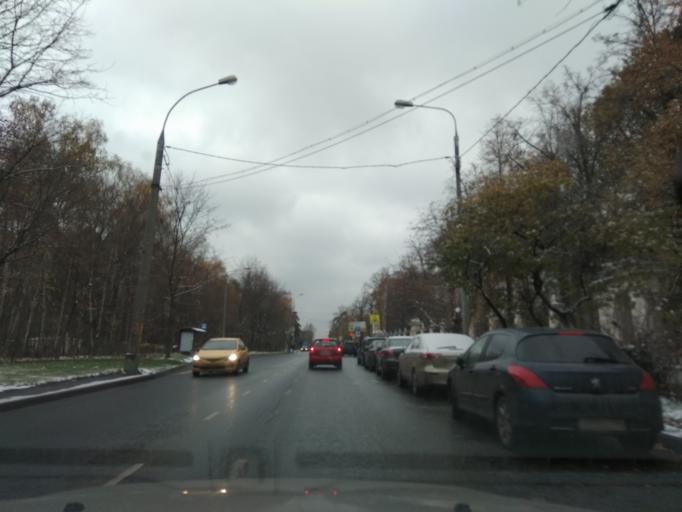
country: RU
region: Moscow
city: Pokrovskoye-Streshnevo
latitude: 55.8038
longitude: 37.4768
